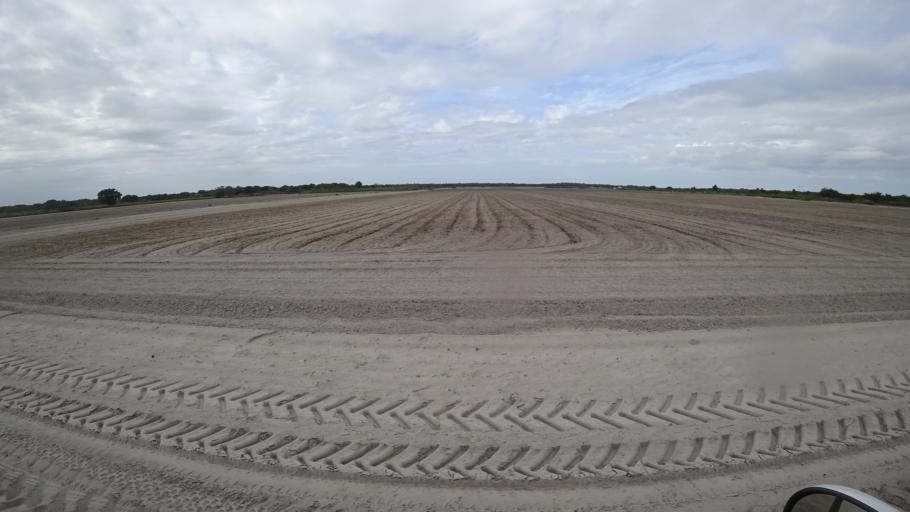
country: US
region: Florida
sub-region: Hillsborough County
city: Wimauma
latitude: 27.5608
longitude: -82.2944
